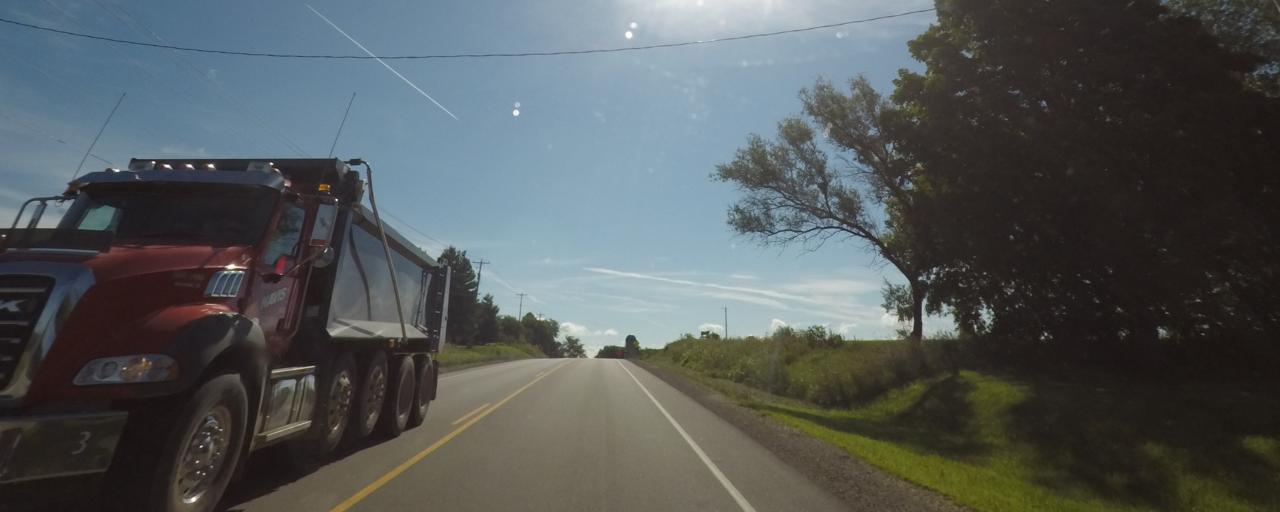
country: US
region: Wisconsin
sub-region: Jefferson County
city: Johnson Creek
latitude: 43.0756
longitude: -88.7292
